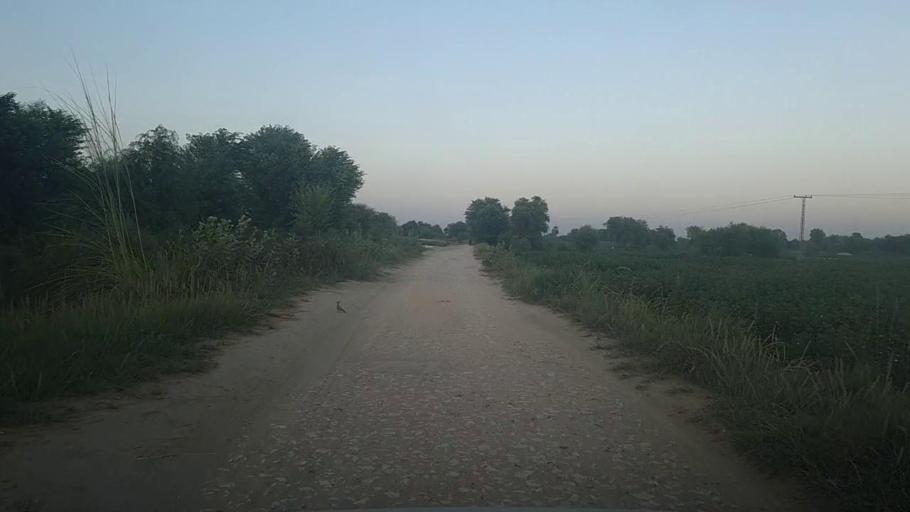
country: PK
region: Sindh
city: Khairpur
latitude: 28.0898
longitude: 69.7271
